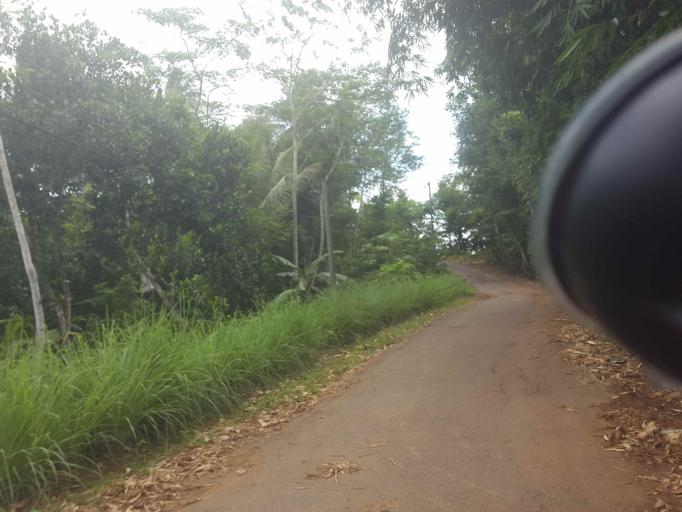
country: ID
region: Central Java
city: Purwokerto
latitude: -7.4420
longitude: 109.1893
